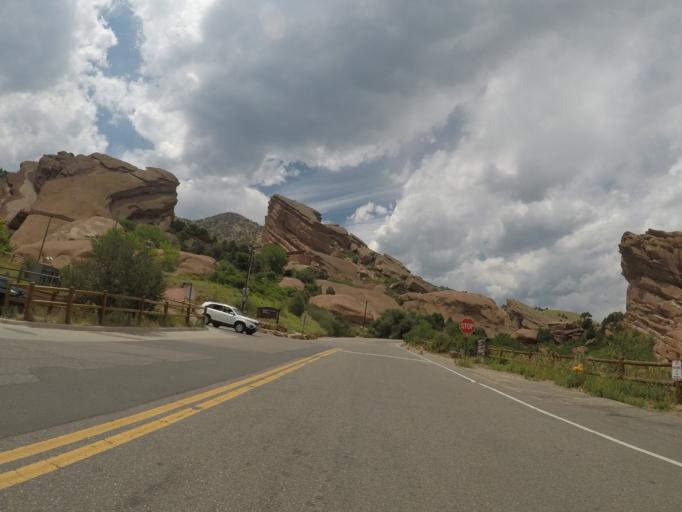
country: US
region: Colorado
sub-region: Jefferson County
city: Indian Hills
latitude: 39.6644
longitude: -105.2028
